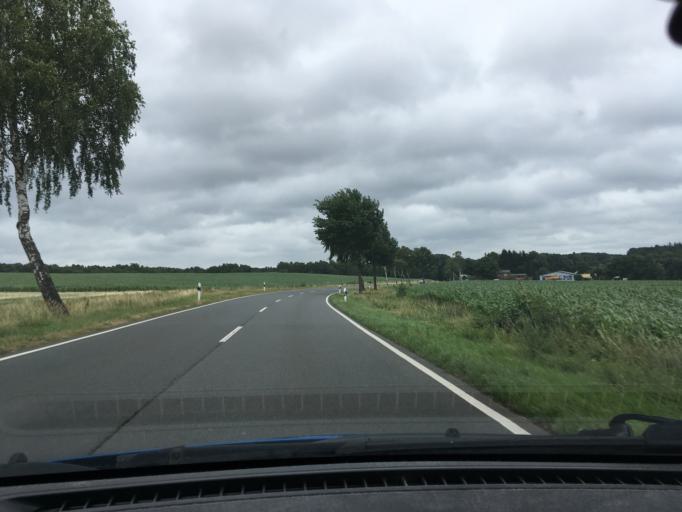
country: DE
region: Lower Saxony
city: Bispingen
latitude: 53.0963
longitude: 9.9831
